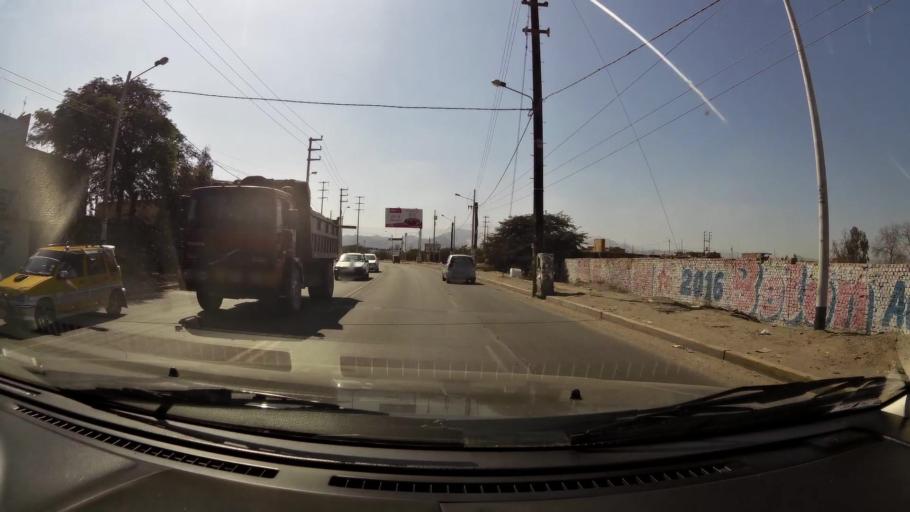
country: PE
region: Ica
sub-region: Provincia de Ica
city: Ica
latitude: -14.0584
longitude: -75.7111
